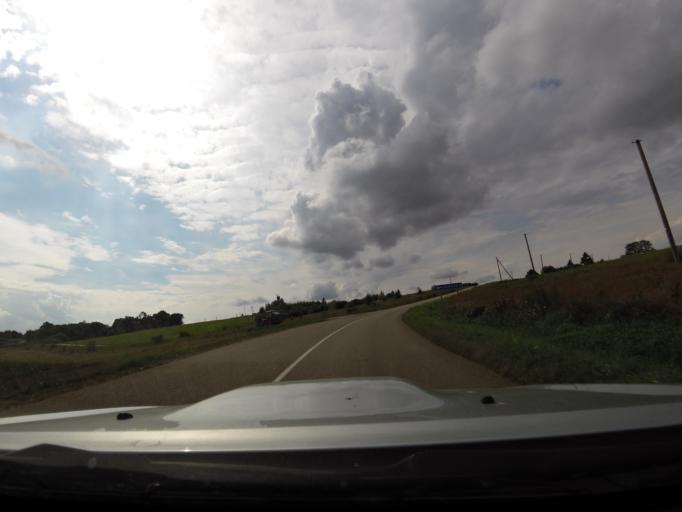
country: LT
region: Vilnius County
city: Elektrenai
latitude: 54.8988
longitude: 24.7146
